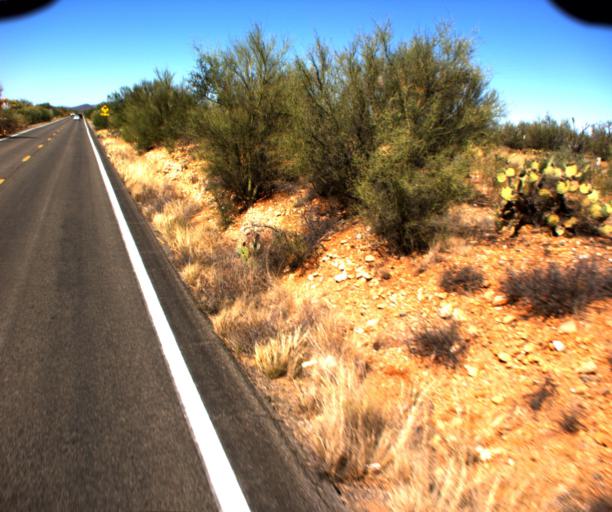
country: US
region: Arizona
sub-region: Pima County
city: Sells
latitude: 31.9650
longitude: -111.7477
